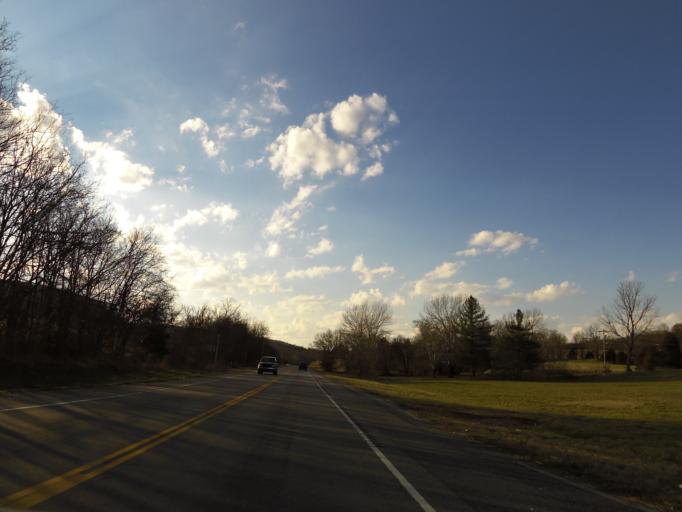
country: US
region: Tennessee
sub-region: Smith County
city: Carthage
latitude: 36.2524
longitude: -86.0390
